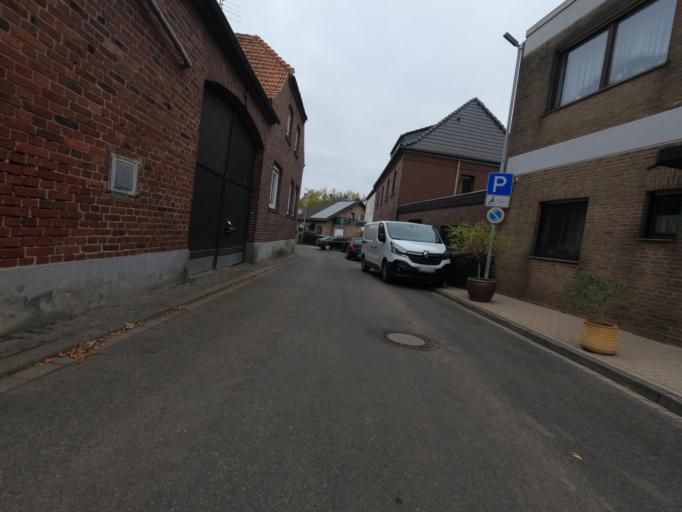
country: DE
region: North Rhine-Westphalia
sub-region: Regierungsbezirk Koln
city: Linnich
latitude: 50.9577
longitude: 6.2885
